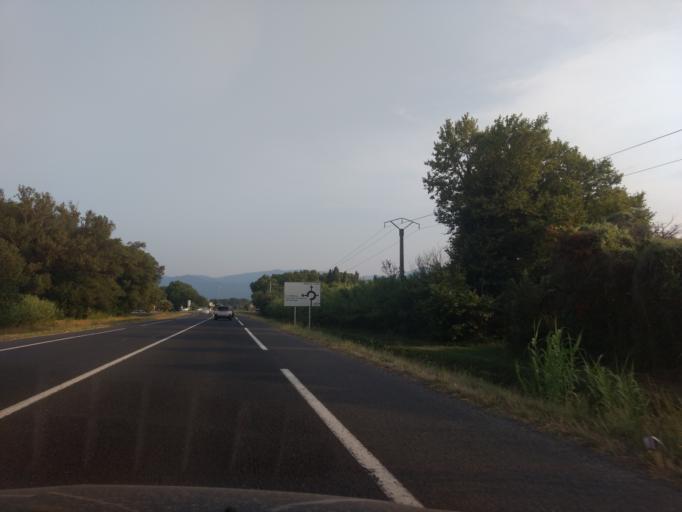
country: FR
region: Languedoc-Roussillon
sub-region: Departement des Pyrenees-Orientales
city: Latour-Bas-Elne
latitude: 42.6097
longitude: 3.0247
